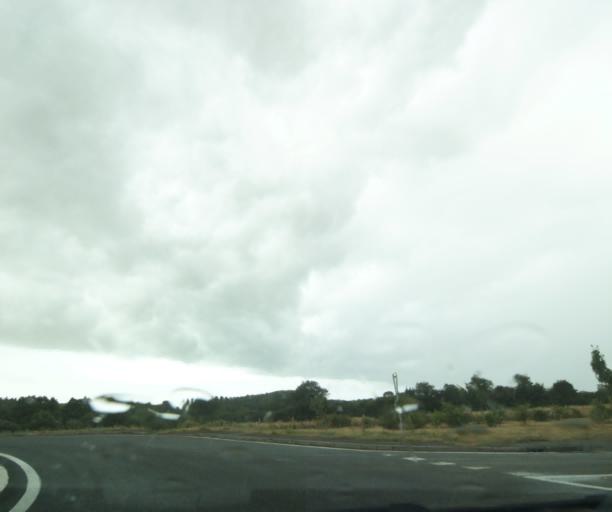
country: FR
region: Pays de la Loire
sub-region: Departement de la Vendee
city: Chateau-d'Olonne
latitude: 46.4803
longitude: -1.7041
